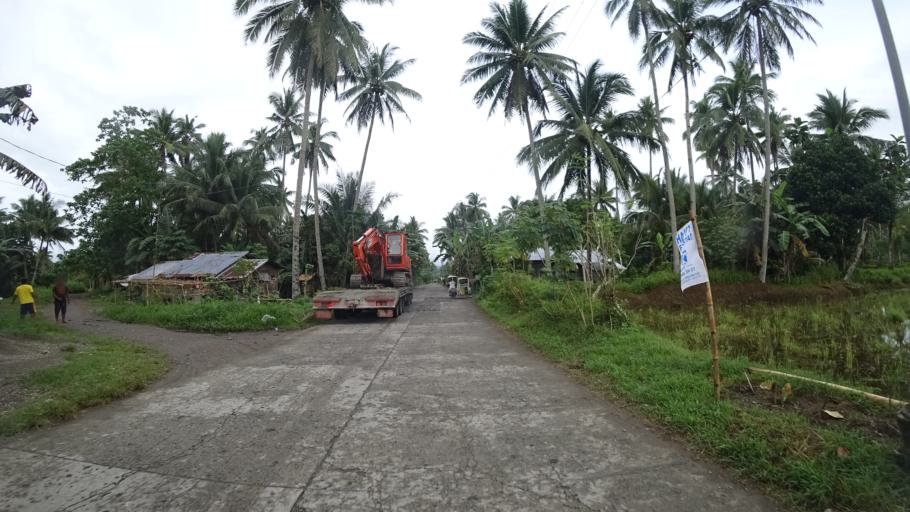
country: PH
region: Eastern Visayas
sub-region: Province of Leyte
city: Bugho
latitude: 10.8188
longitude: 124.9497
